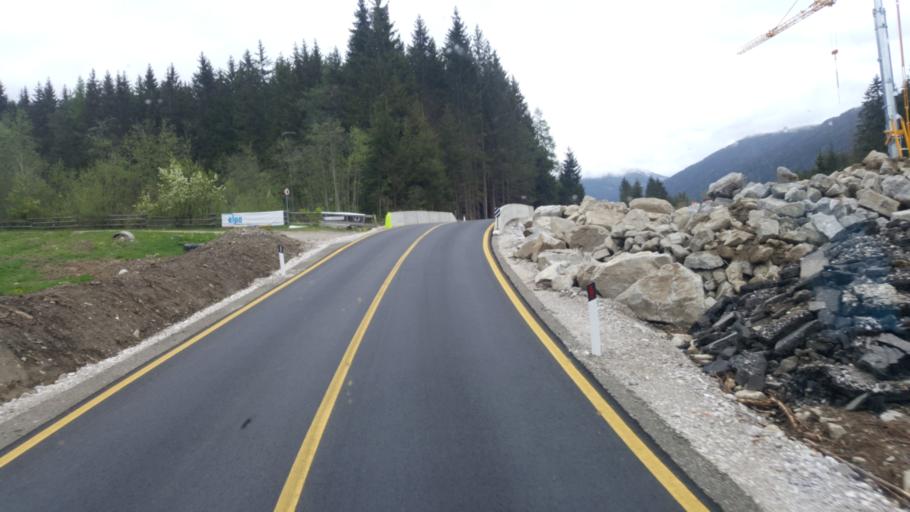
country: IT
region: Trentino-Alto Adige
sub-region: Bolzano
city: Monguelfo
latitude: 46.7663
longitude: 12.1261
